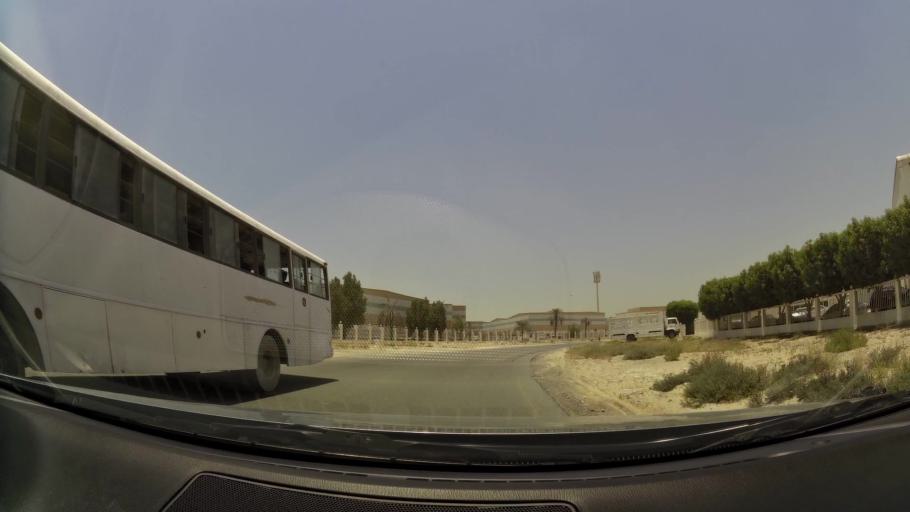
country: AE
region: Dubai
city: Dubai
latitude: 24.9856
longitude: 55.1656
